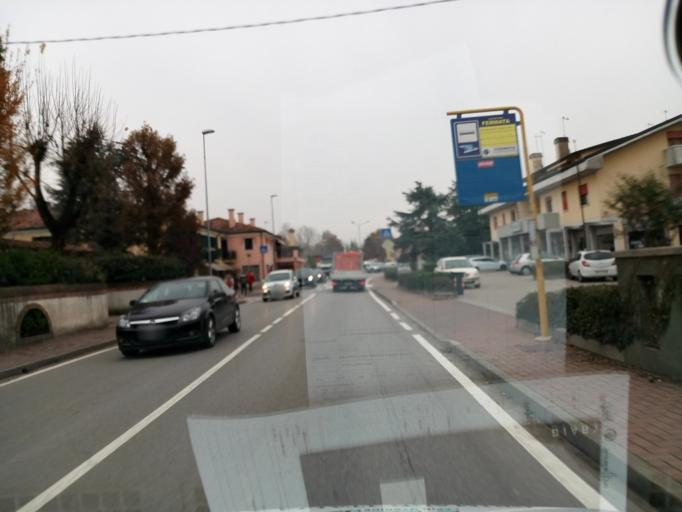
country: IT
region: Veneto
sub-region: Provincia di Padova
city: Piombino Dese
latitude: 45.6044
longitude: 12.0026
